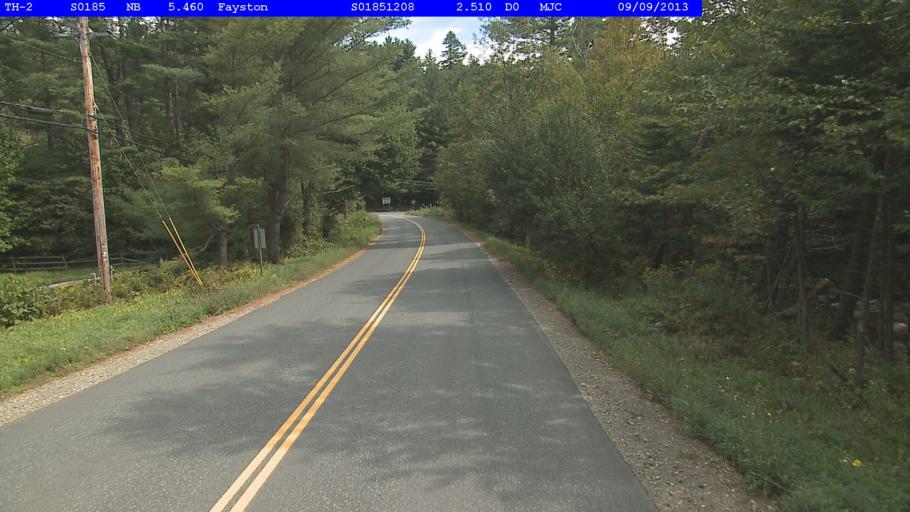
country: US
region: Vermont
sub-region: Washington County
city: Waterbury
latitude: 44.1850
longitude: -72.8732
